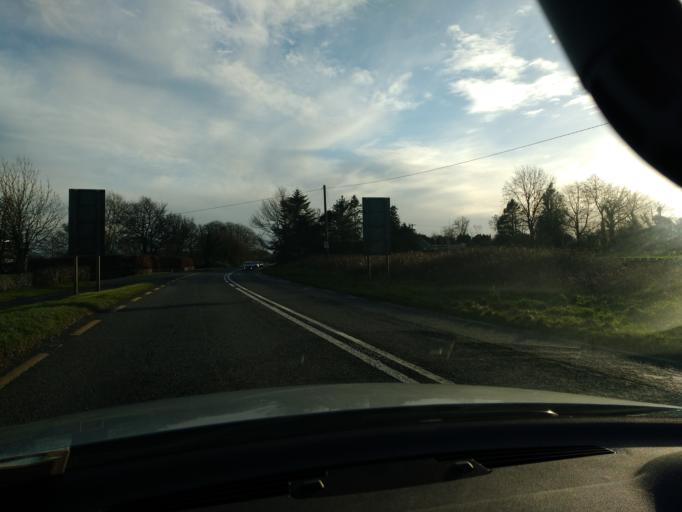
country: IE
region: Munster
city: Thurles
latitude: 52.6560
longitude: -7.7995
